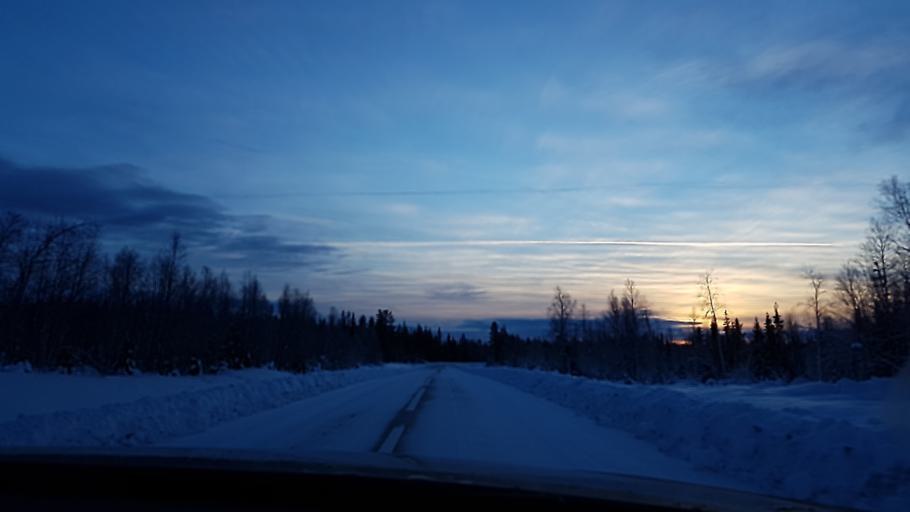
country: SE
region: Norrbotten
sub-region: Jokkmokks Kommun
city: Jokkmokk
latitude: 66.1088
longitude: 20.0520
